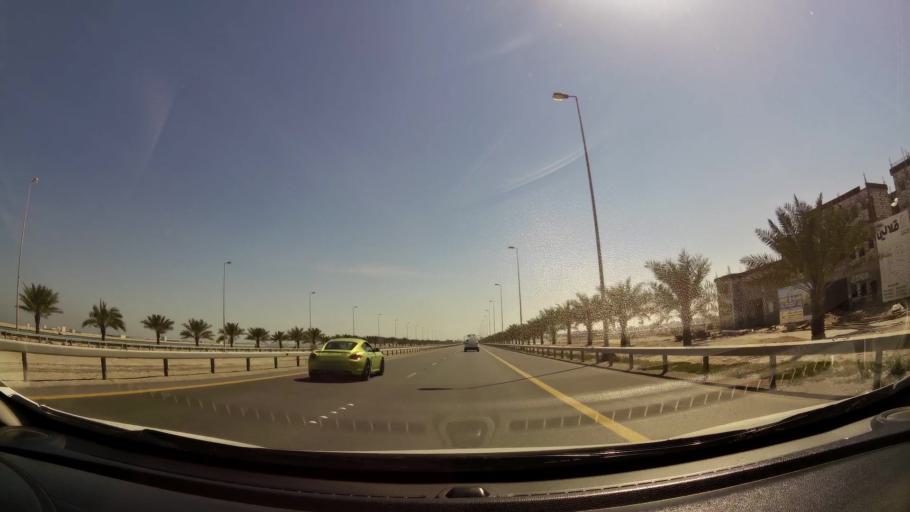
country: BH
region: Muharraq
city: Al Hadd
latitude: 26.2633
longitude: 50.6612
